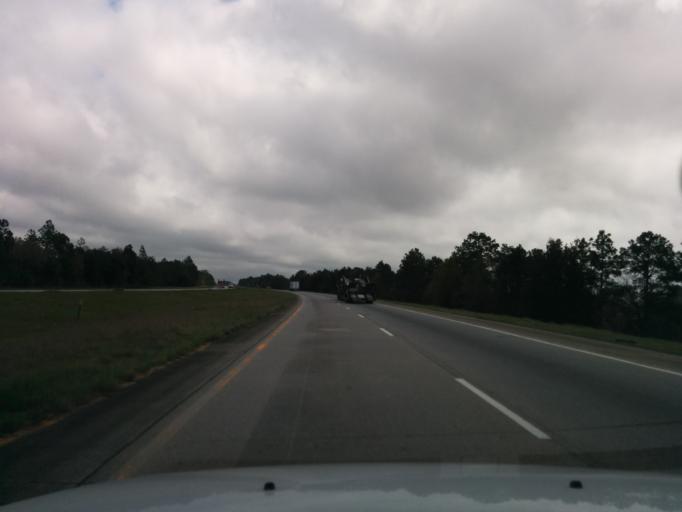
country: US
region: Georgia
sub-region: Toombs County
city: Lyons
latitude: 32.3911
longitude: -82.2903
